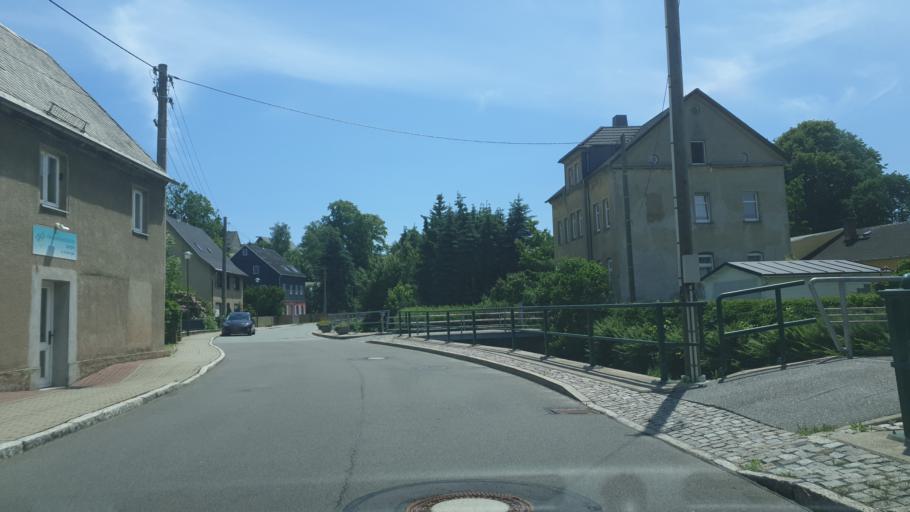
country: DE
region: Saxony
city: Niederdorf
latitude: 50.7277
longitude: 12.7890
